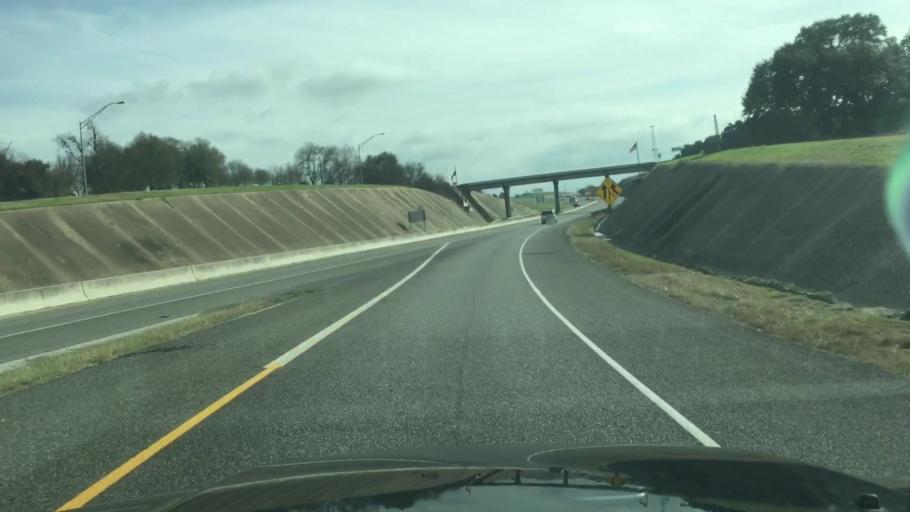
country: US
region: Texas
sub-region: Washington County
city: Brenham
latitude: 30.1642
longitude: -96.4237
